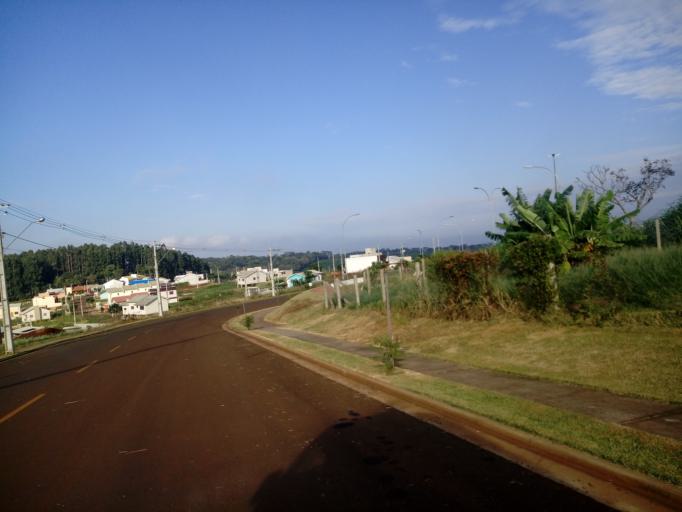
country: BR
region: Santa Catarina
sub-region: Chapeco
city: Chapeco
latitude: -27.0887
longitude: -52.7107
